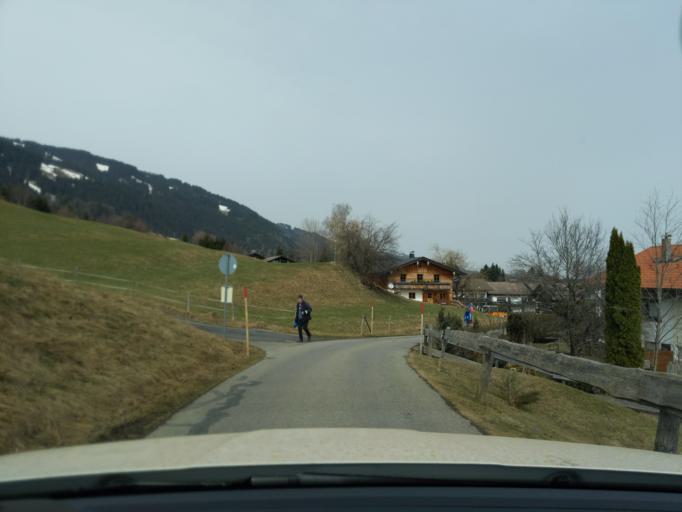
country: DE
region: Bavaria
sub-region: Swabia
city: Obermaiselstein
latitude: 47.4461
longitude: 10.2350
